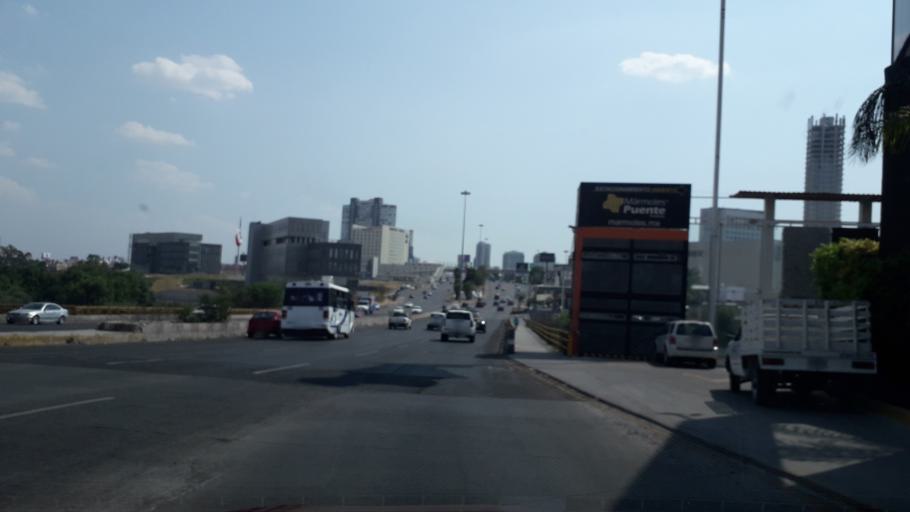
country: MX
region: Puebla
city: Puebla
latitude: 19.0365
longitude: -98.2264
